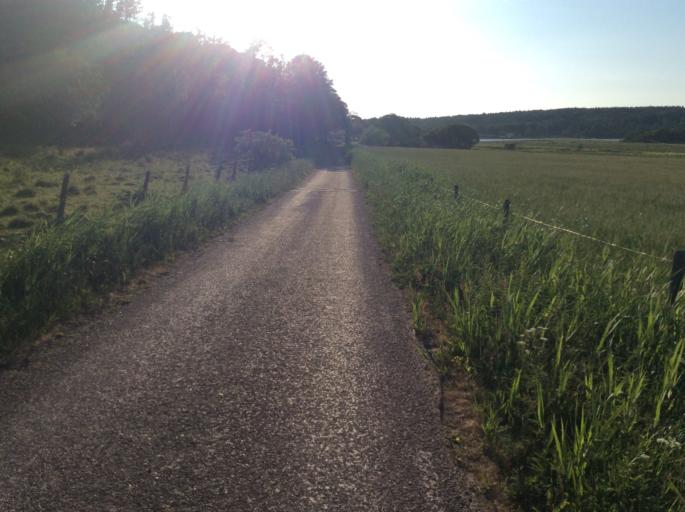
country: SE
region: Vaestra Goetaland
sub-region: Goteborg
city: Majorna
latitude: 57.7961
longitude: 11.8632
